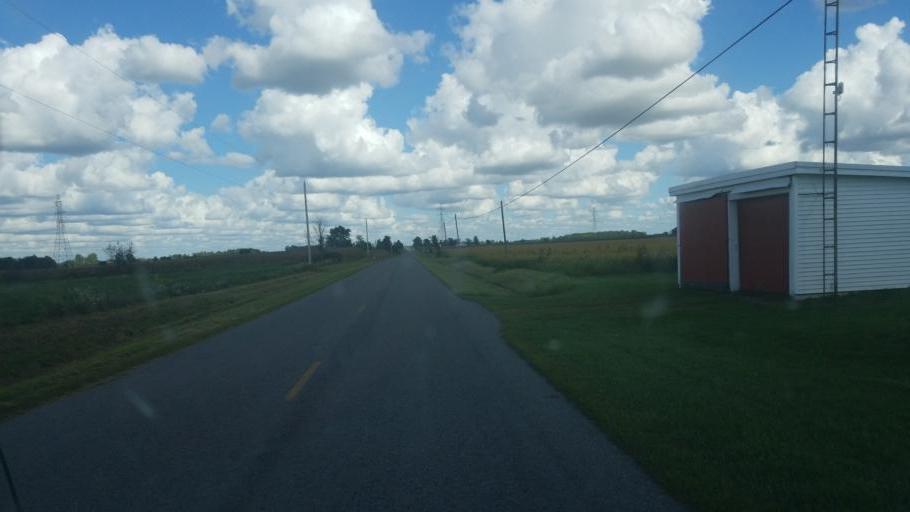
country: US
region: Ohio
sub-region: Logan County
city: Northwood
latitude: 40.5031
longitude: -83.6079
